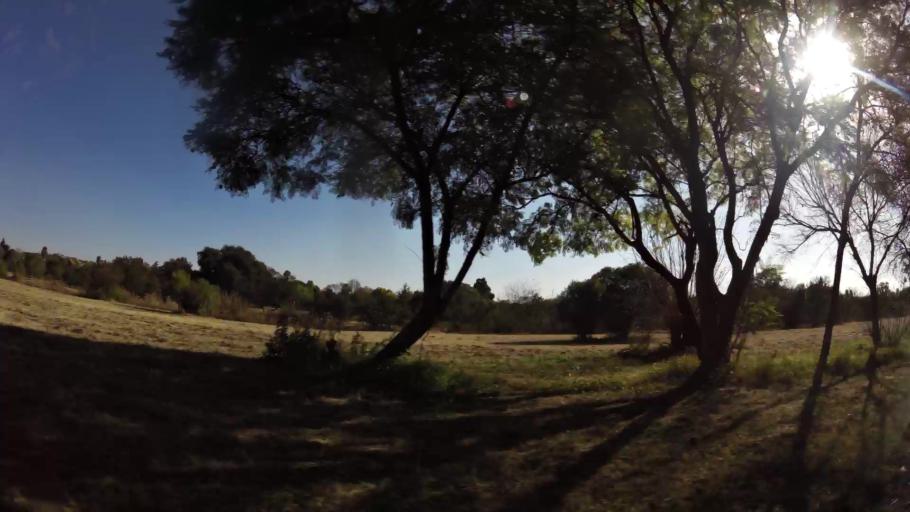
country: ZA
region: Gauteng
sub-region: City of Tshwane Metropolitan Municipality
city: Pretoria
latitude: -25.7291
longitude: 28.2628
